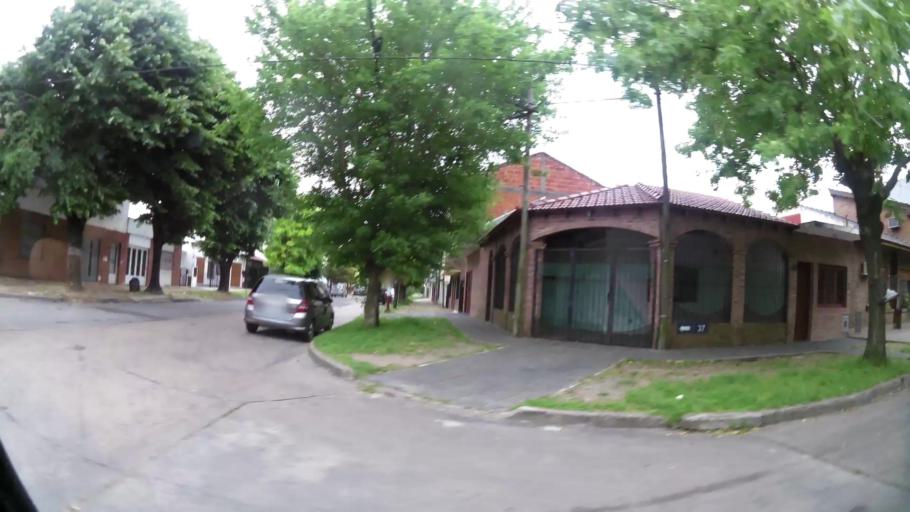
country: AR
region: Buenos Aires
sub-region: Partido de La Plata
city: La Plata
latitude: -34.9244
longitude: -57.9848
